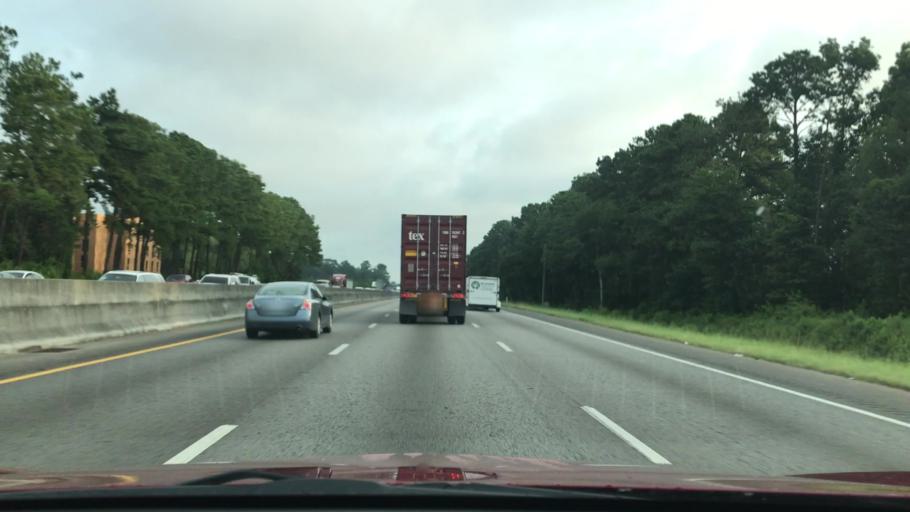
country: US
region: South Carolina
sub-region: Berkeley County
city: Ladson
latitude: 32.9724
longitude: -80.0758
